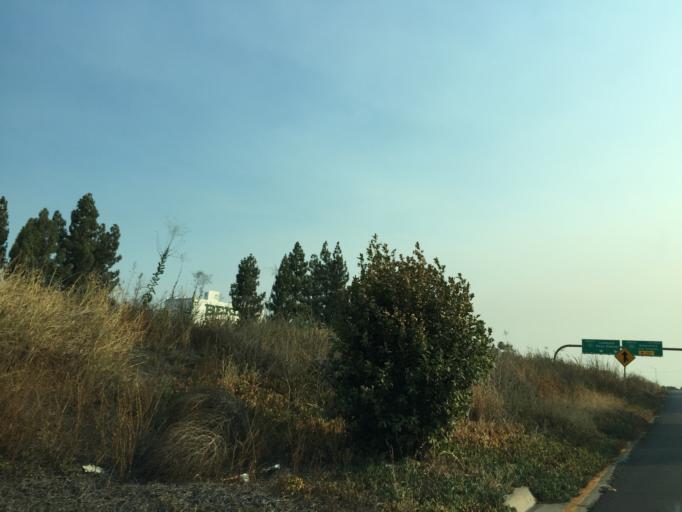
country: US
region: California
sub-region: Fresno County
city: Fresno
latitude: 36.7297
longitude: -119.7822
